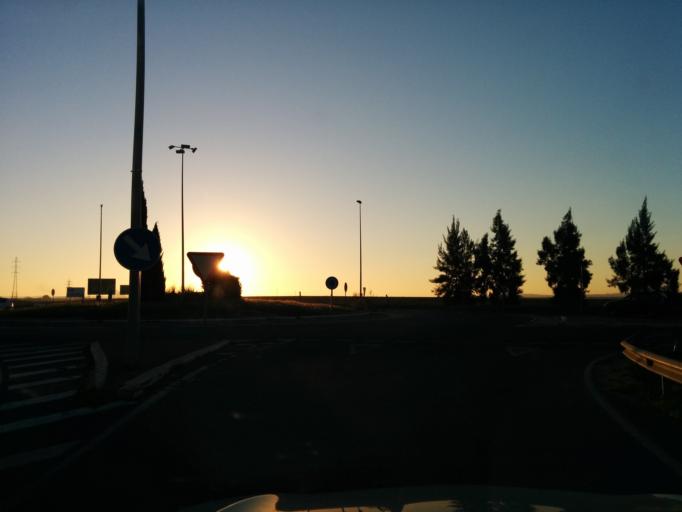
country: ES
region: Andalusia
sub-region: Provincia de Sevilla
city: Sevilla
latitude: 37.3726
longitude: -5.9249
